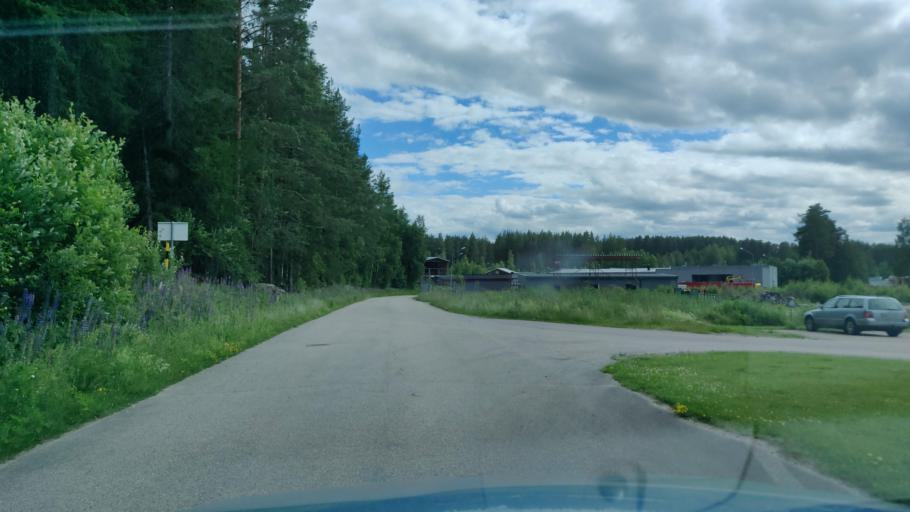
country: SE
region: Vaermland
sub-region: Hagfors Kommun
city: Hagfors
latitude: 60.0458
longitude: 13.7124
